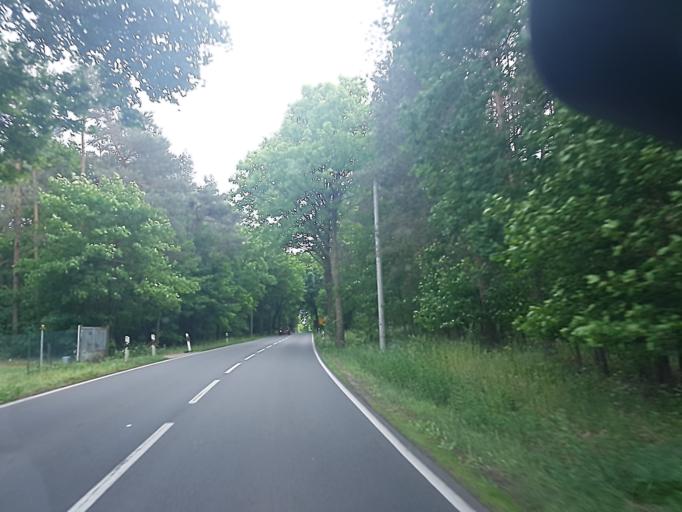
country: DE
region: Saxony-Anhalt
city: Nudersdorf
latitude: 51.9225
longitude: 12.6056
